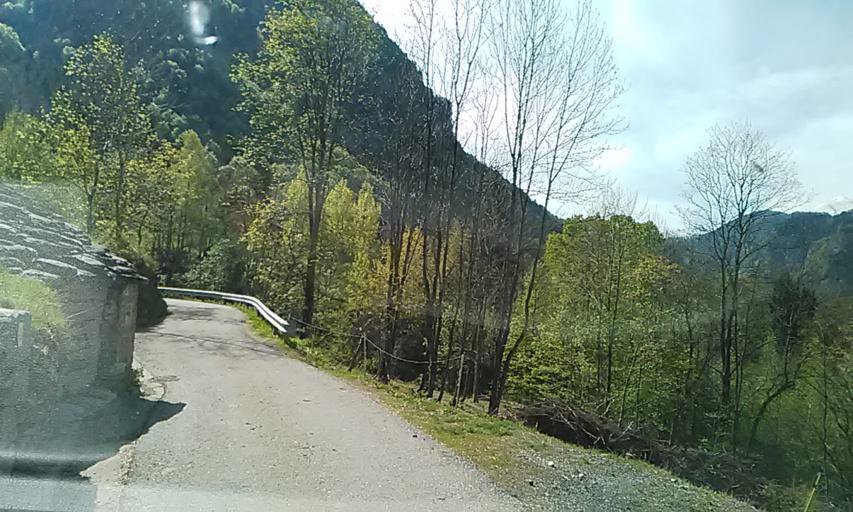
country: IT
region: Piedmont
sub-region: Provincia di Vercelli
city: Mollia
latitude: 45.8156
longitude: 8.0335
